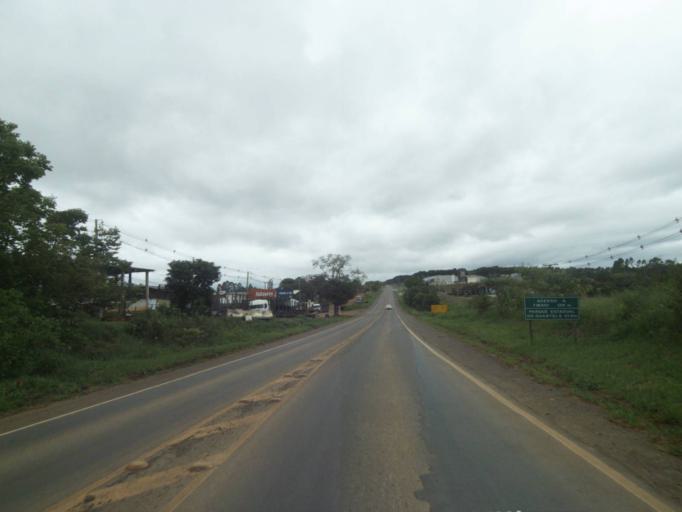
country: BR
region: Parana
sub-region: Telemaco Borba
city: Telemaco Borba
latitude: -24.3838
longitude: -50.6743
